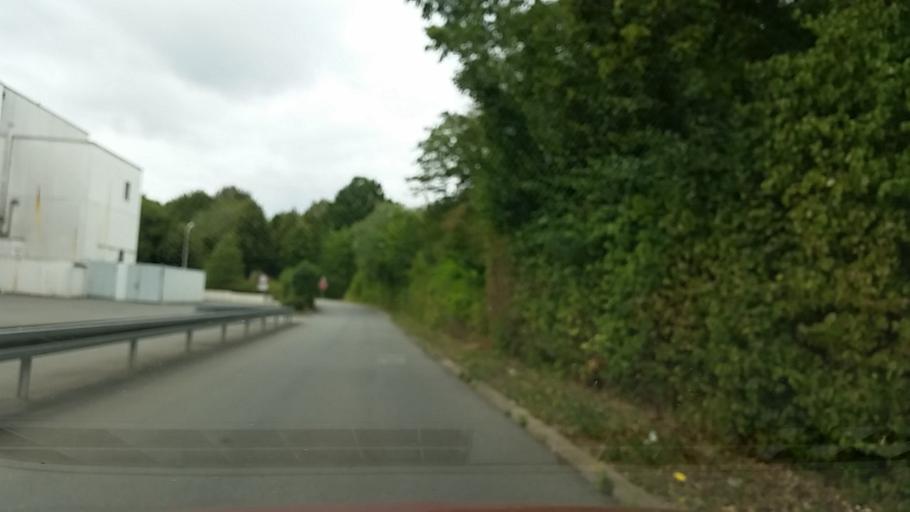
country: DE
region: Lower Saxony
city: Goslar
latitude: 51.9170
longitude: 10.4495
